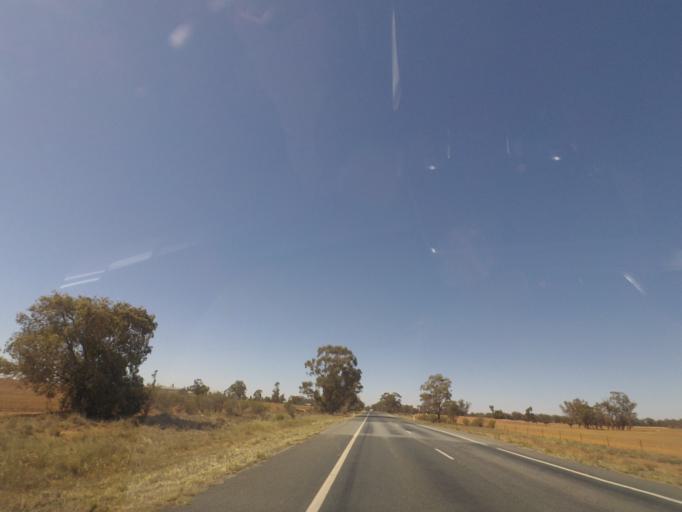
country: AU
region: New South Wales
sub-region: Bland
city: West Wyalong
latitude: -34.1892
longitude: 147.1120
